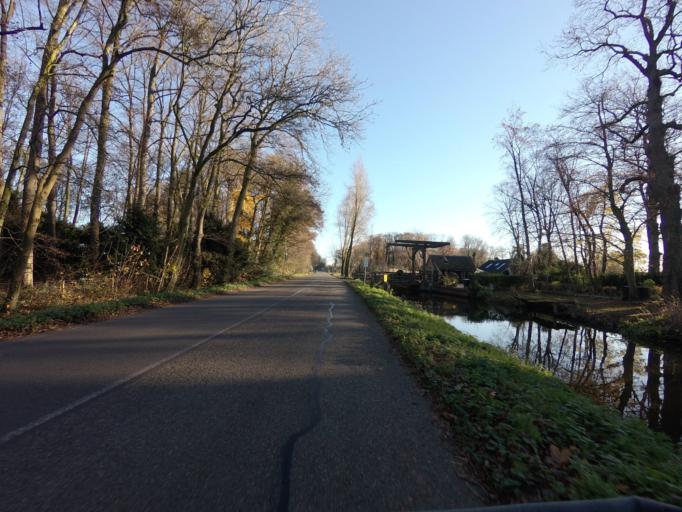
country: NL
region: Utrecht
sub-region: Stichtse Vecht
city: Vreeland
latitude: 52.2337
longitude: 4.9929
